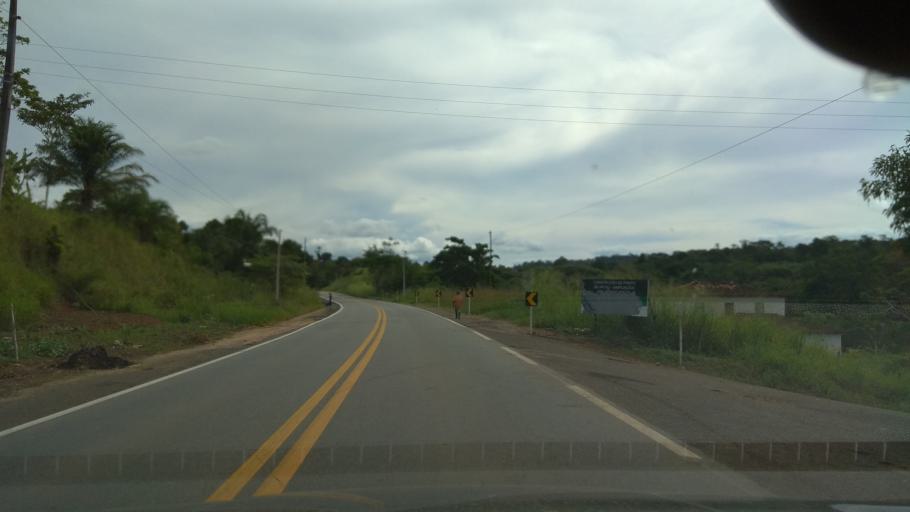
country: BR
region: Bahia
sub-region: Ubata
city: Ubata
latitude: -14.1938
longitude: -39.5504
